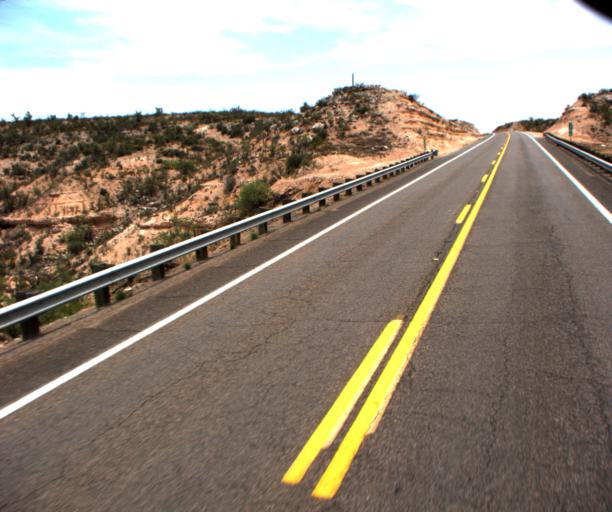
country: US
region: Arizona
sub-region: Graham County
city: Bylas
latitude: 33.2234
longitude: -110.2263
